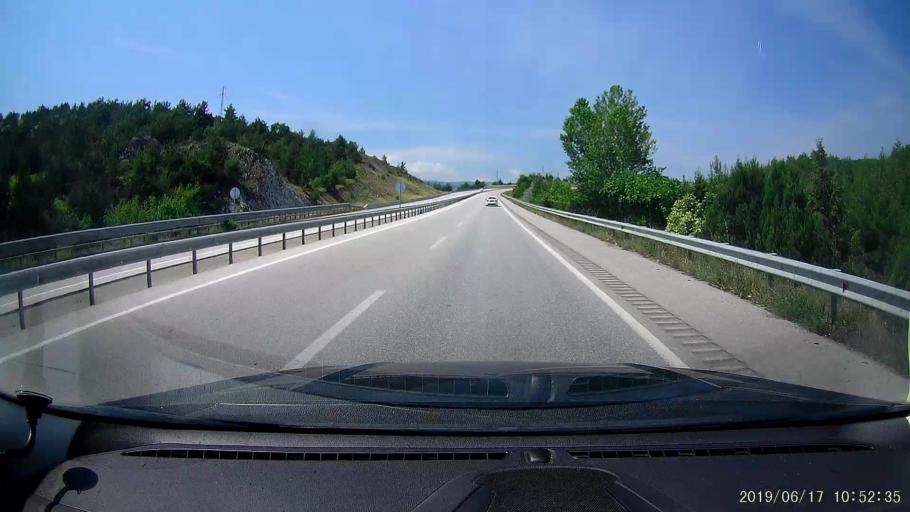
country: TR
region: Corum
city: Hacihamza
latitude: 41.0868
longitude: 34.3397
